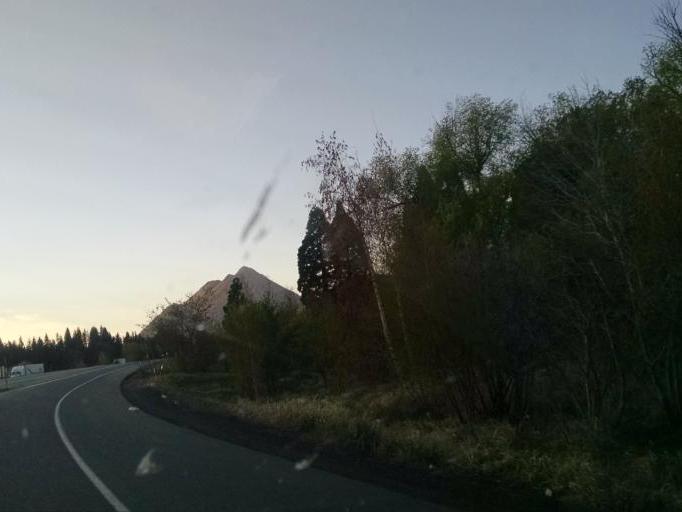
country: US
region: California
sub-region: Siskiyou County
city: Mount Shasta
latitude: 41.3118
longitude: -122.3206
